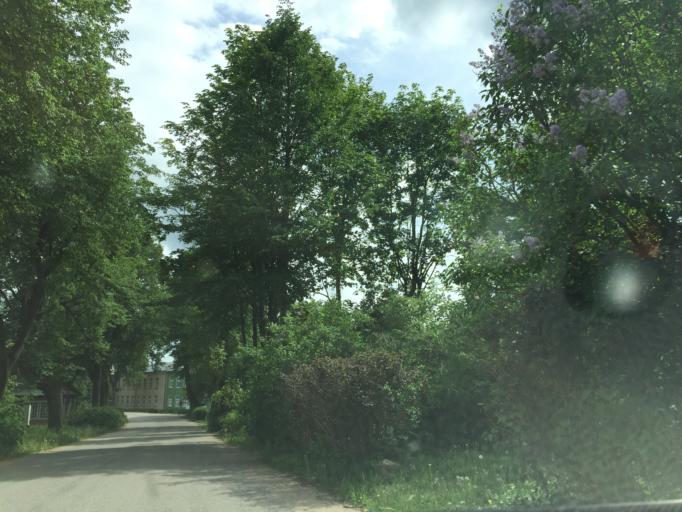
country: LV
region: Dagda
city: Dagda
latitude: 56.0248
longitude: 27.6221
